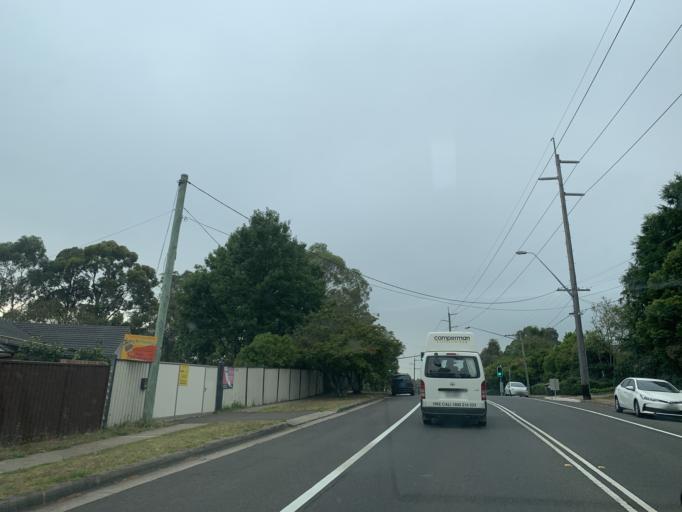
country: AU
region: New South Wales
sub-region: The Hills Shire
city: West Pennant
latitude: -33.7300
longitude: 151.0420
